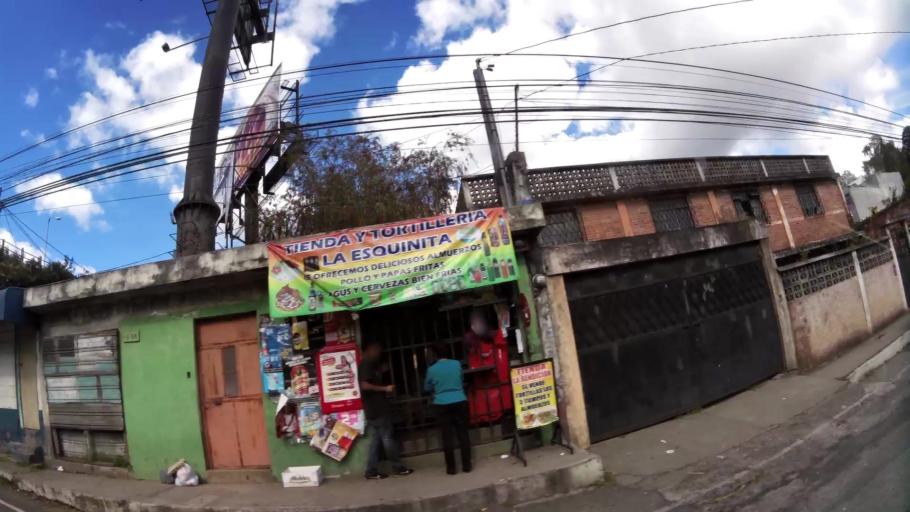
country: GT
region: Guatemala
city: Mixco
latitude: 14.5926
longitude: -90.5648
